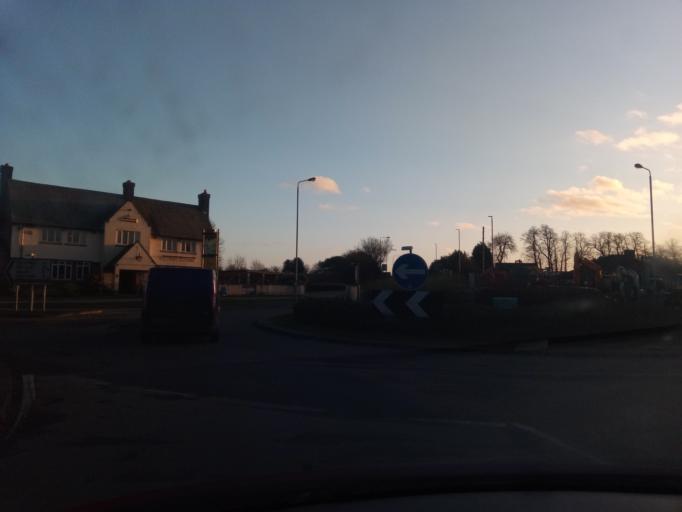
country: GB
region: England
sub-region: Nottinghamshire
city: Farnsfield
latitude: 53.1073
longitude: -1.0637
